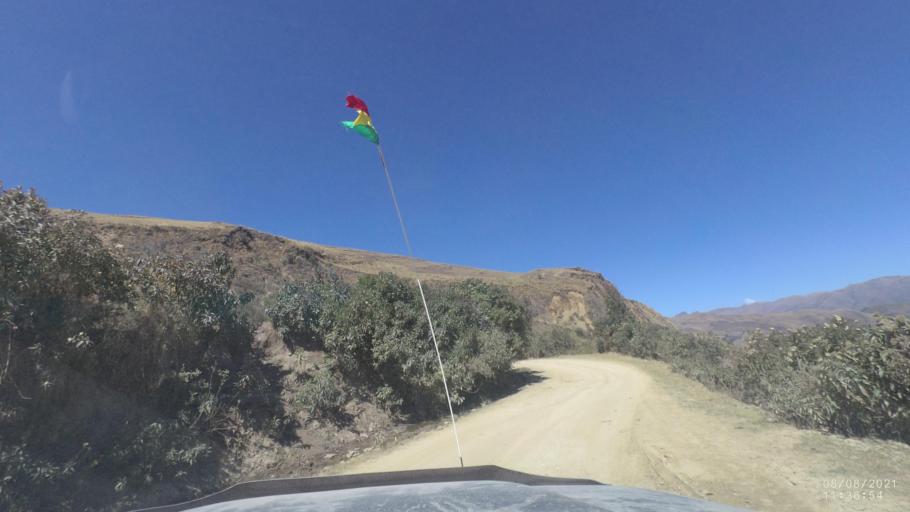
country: BO
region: Cochabamba
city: Colchani
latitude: -16.7830
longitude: -66.6458
